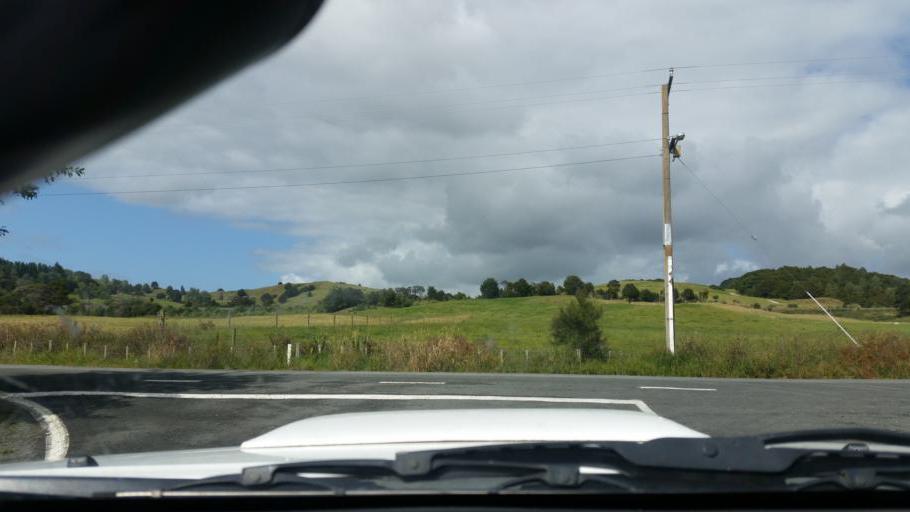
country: NZ
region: Auckland
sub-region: Auckland
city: Wellsford
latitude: -36.1318
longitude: 174.3595
